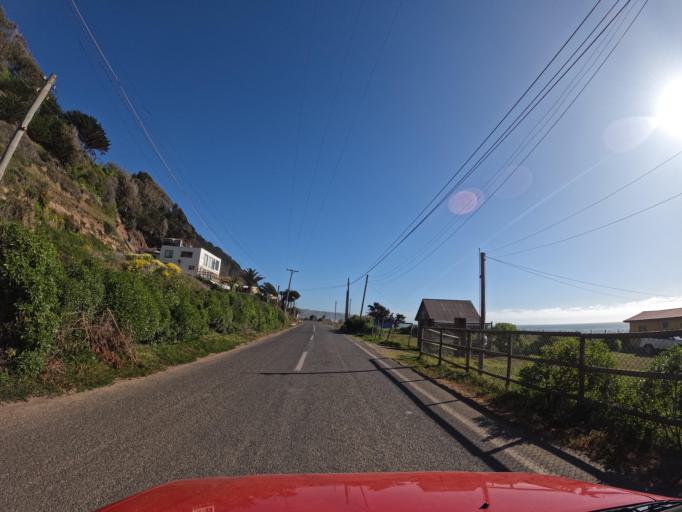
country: CL
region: Maule
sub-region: Provincia de Talca
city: Constitucion
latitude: -34.8582
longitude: -72.1459
